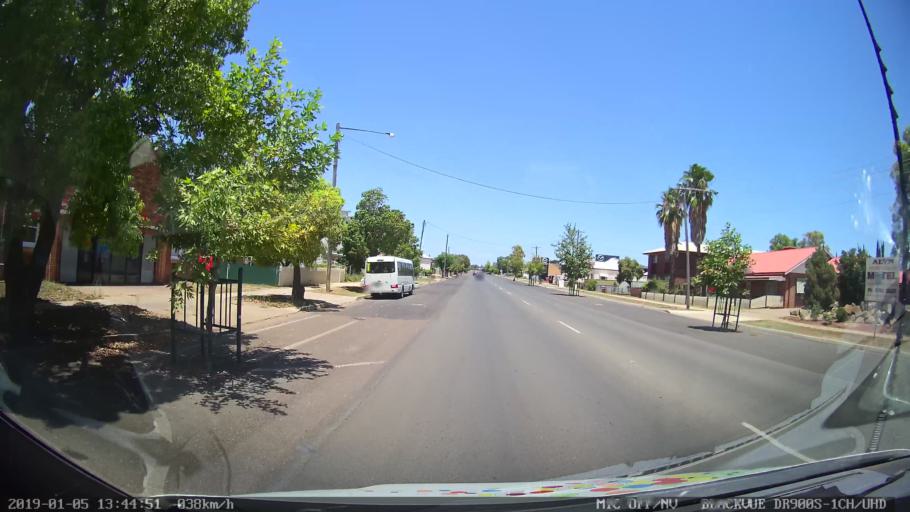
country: AU
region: New South Wales
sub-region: Gunnedah
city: Gunnedah
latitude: -30.9808
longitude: 150.2586
